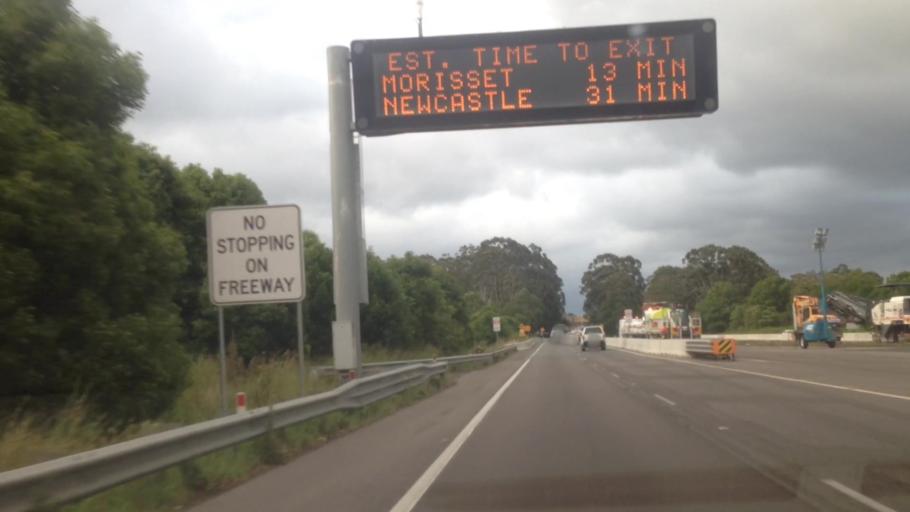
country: AU
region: New South Wales
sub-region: Wyong Shire
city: Chittaway Bay
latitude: -33.2820
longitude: 151.4058
